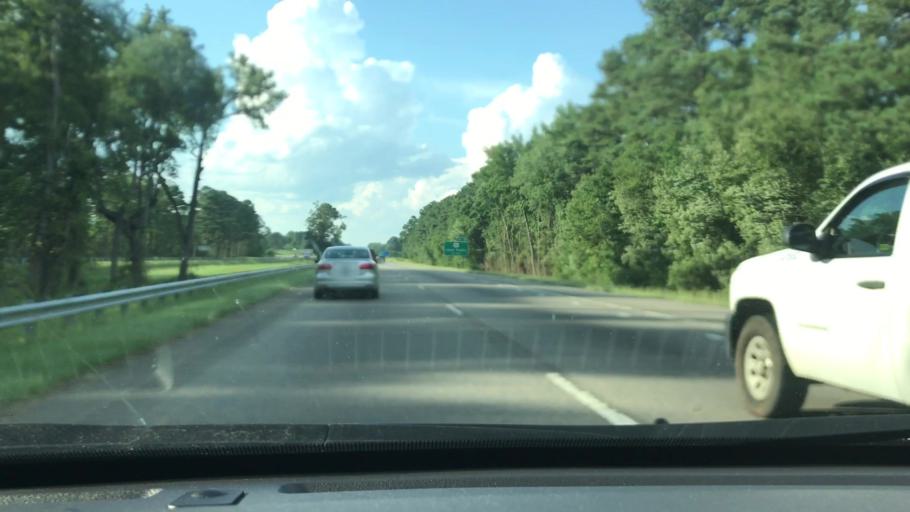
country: US
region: North Carolina
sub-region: Robeson County
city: Lumberton
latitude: 34.7119
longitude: -78.9975
